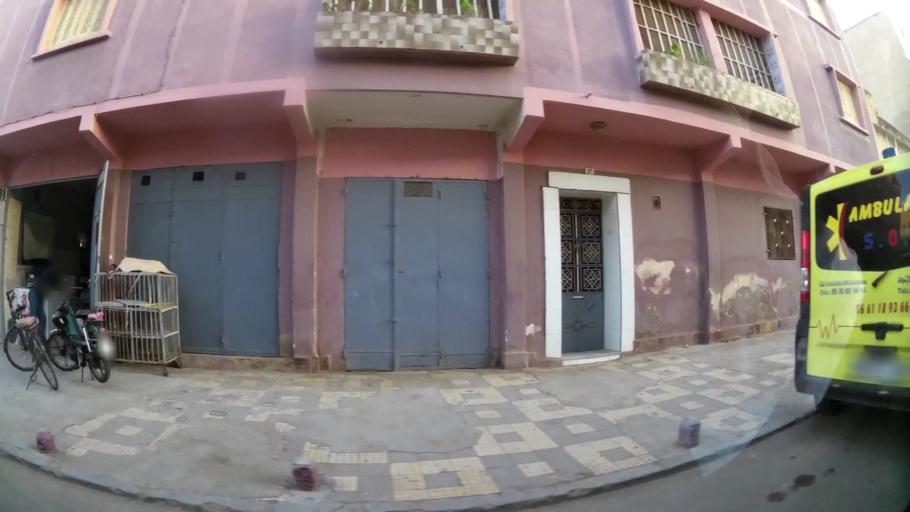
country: MA
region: Oriental
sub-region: Oujda-Angad
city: Oujda
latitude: 34.7023
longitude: -1.9207
